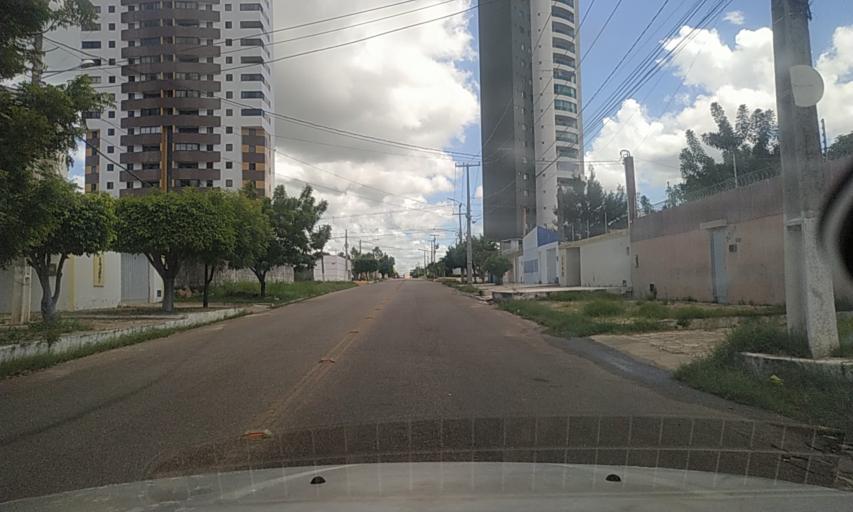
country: BR
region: Rio Grande do Norte
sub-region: Mossoro
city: Mossoro
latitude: -5.1794
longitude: -37.3613
